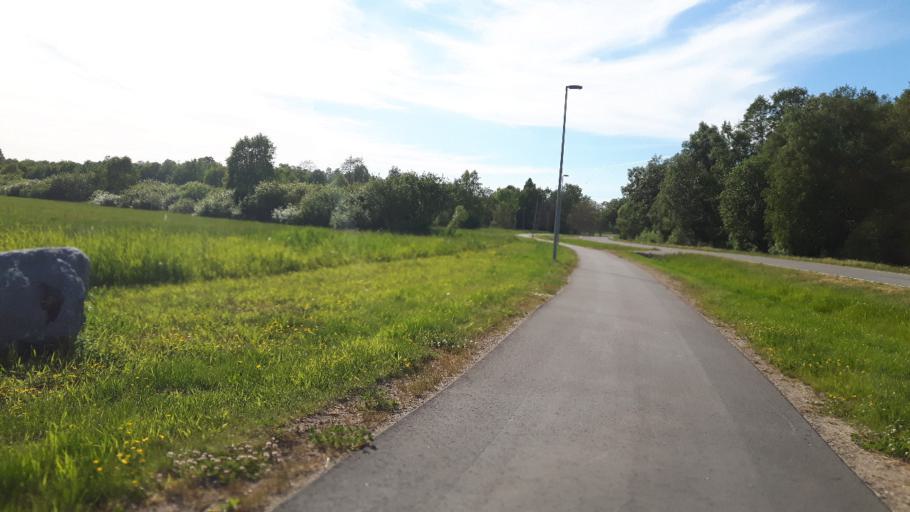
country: EE
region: Harju
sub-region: Joelaehtme vald
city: Loo
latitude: 59.4278
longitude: 24.9873
